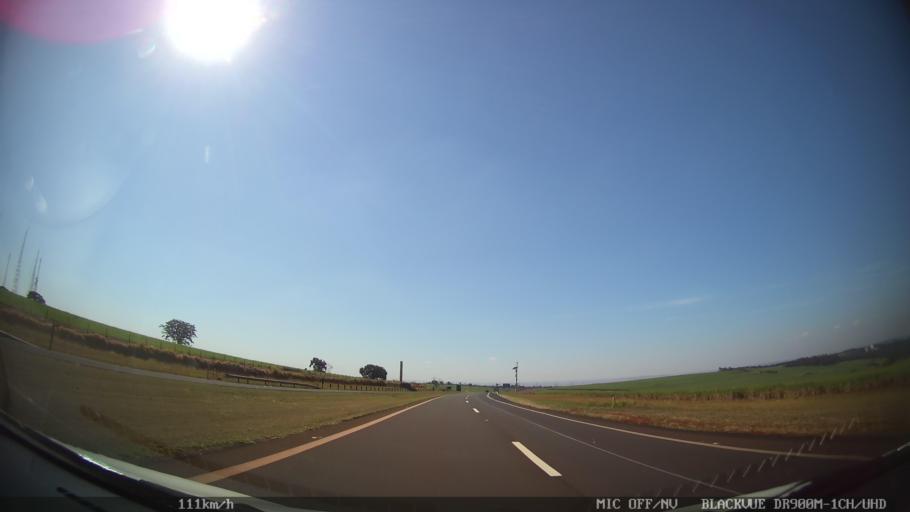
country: BR
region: Sao Paulo
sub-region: Ribeirao Preto
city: Ribeirao Preto
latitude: -21.1626
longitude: -47.8979
